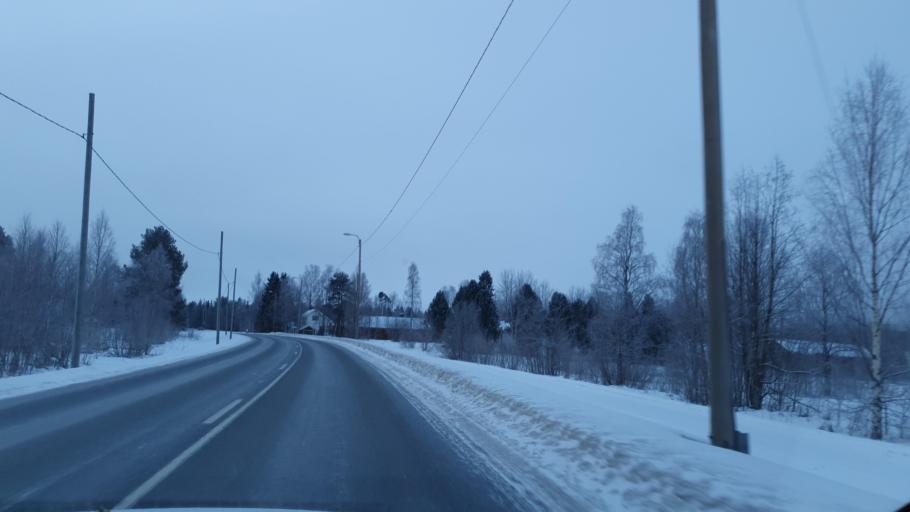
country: FI
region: Lapland
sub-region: Torniolaakso
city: Pello
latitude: 66.6358
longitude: 23.8770
